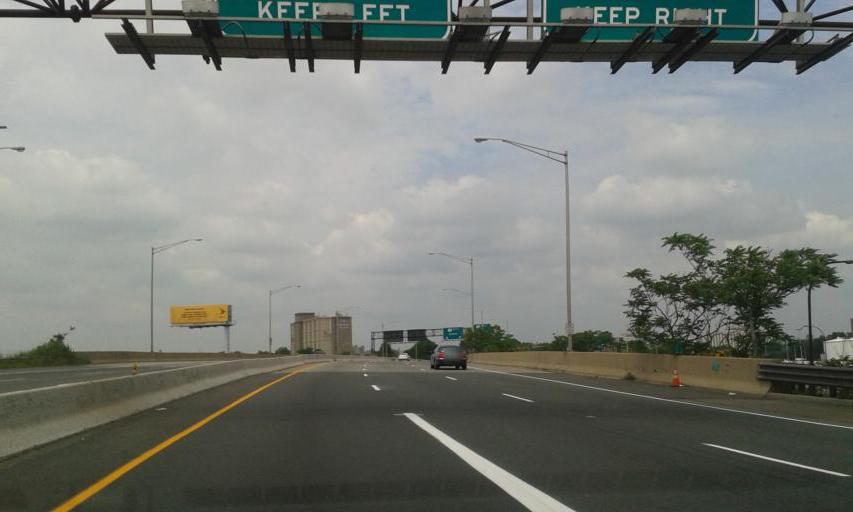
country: US
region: New Jersey
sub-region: Union County
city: Elizabeth
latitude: 40.6756
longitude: -74.1904
